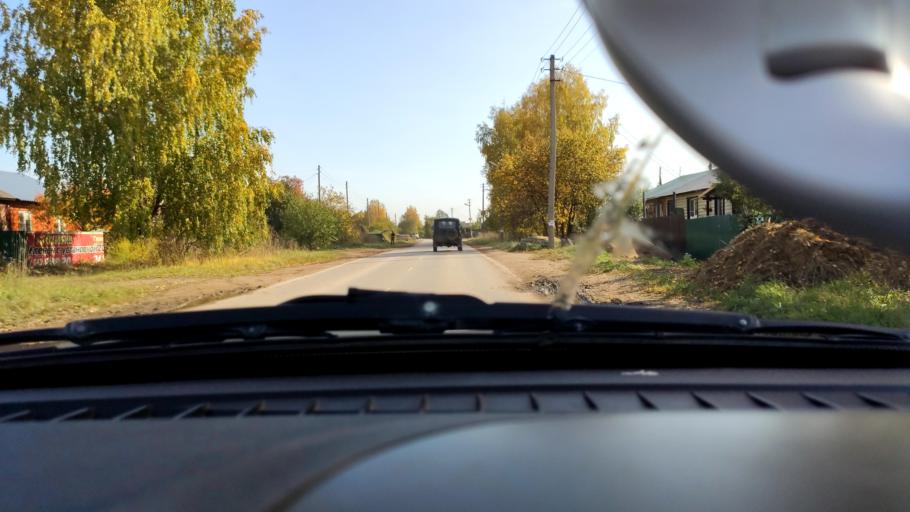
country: RU
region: Perm
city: Overyata
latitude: 58.0576
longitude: 55.8899
